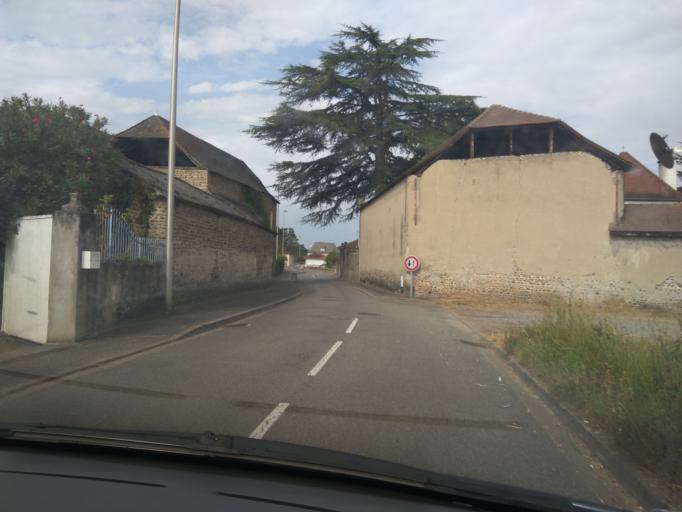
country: FR
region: Aquitaine
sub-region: Departement des Pyrenees-Atlantiques
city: Mourenx
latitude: 43.3649
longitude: -0.5797
